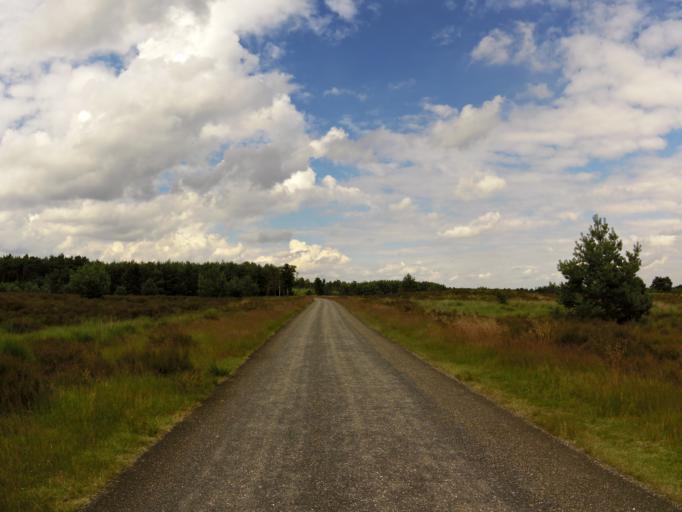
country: NL
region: North Brabant
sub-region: Gemeente Valkenswaard
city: Valkenswaard
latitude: 51.3081
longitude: 5.5080
